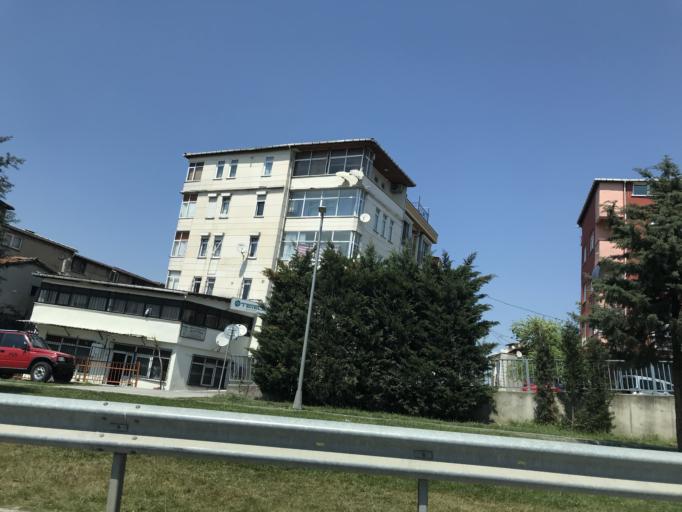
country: TR
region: Istanbul
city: Sisli
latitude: 41.0573
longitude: 28.9603
